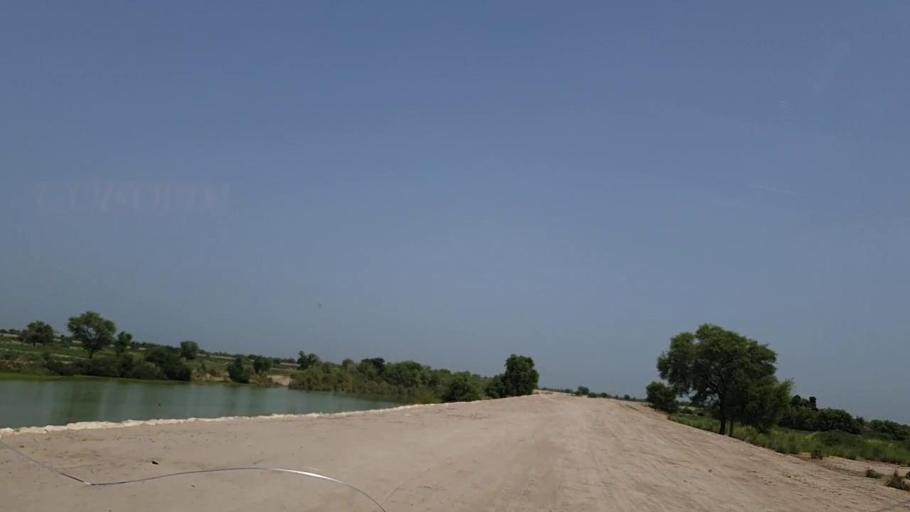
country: PK
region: Sindh
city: Kandiaro
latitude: 27.0590
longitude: 68.1289
